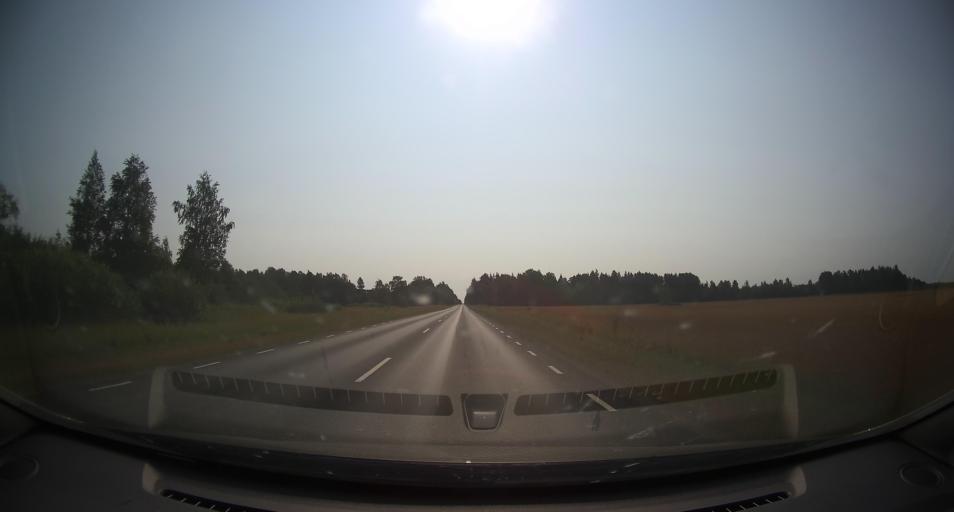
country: EE
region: Paernumaa
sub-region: Audru vald
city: Audru
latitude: 58.4406
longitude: 24.2475
